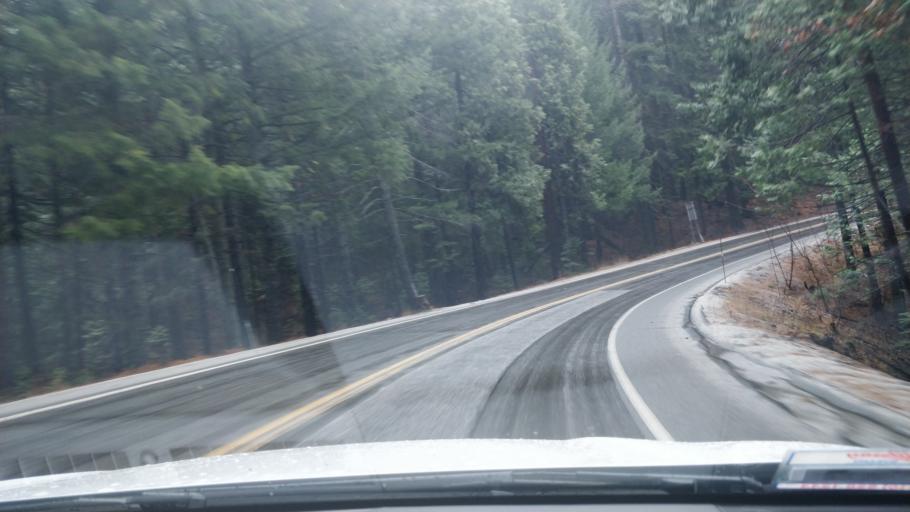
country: US
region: California
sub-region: Nevada County
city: Nevada City
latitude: 39.3242
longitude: -120.8327
